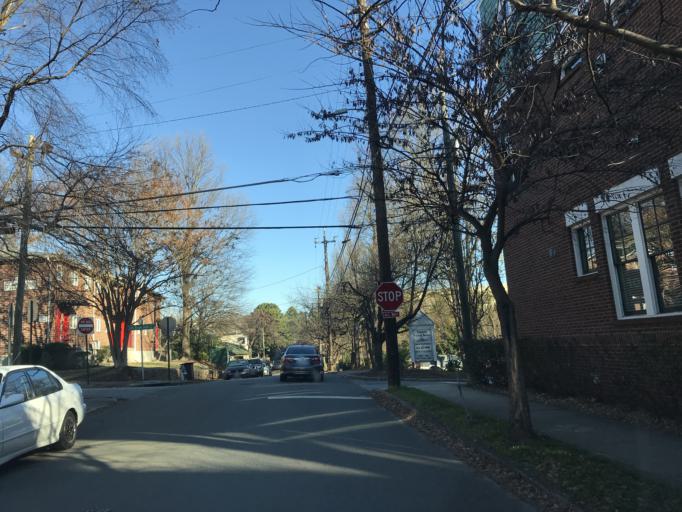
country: US
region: Georgia
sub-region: Fulton County
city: Atlanta
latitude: 33.7592
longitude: -84.3656
